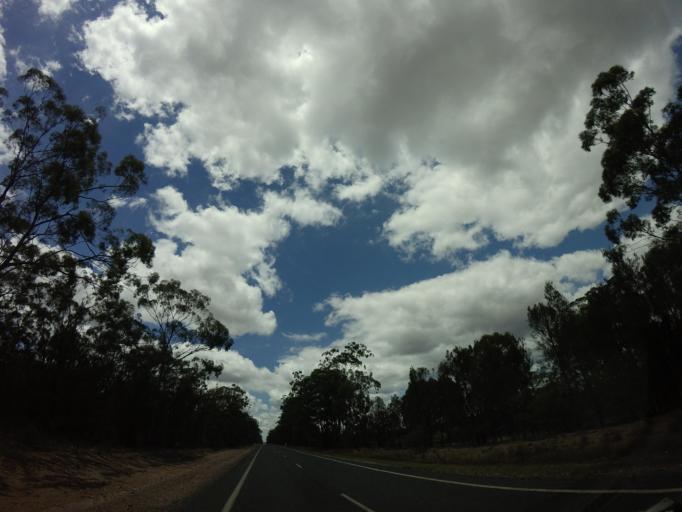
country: AU
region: Queensland
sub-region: Goondiwindi
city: Goondiwindi
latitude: -28.0222
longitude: 150.8502
